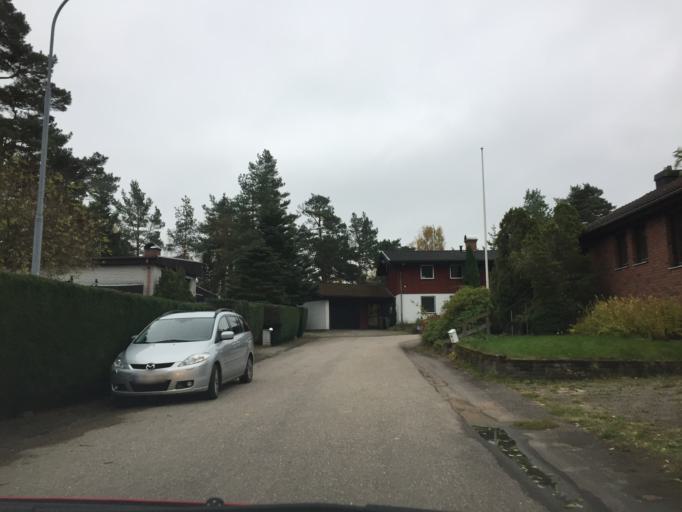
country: SE
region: Vaestra Goetaland
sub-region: Trollhattan
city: Trollhattan
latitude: 58.2627
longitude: 12.2835
